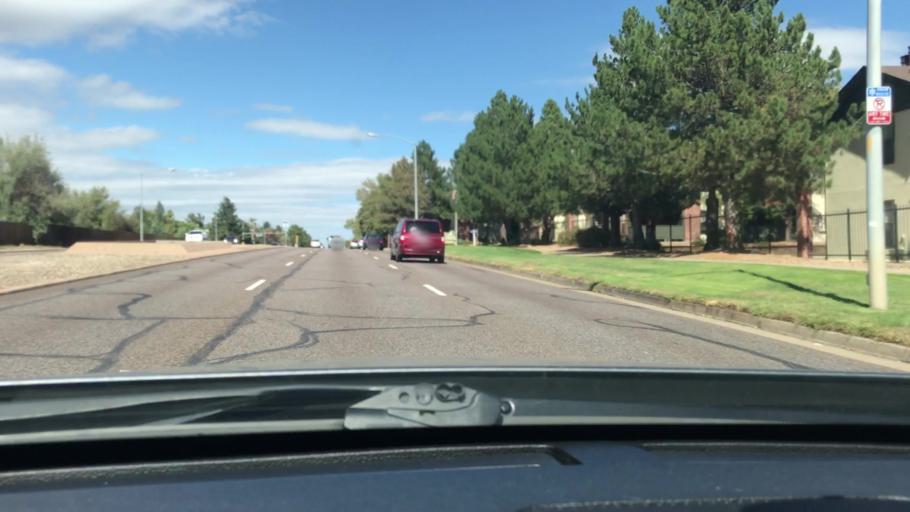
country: US
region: Colorado
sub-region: Arapahoe County
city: Dove Valley
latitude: 39.6363
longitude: -104.8102
